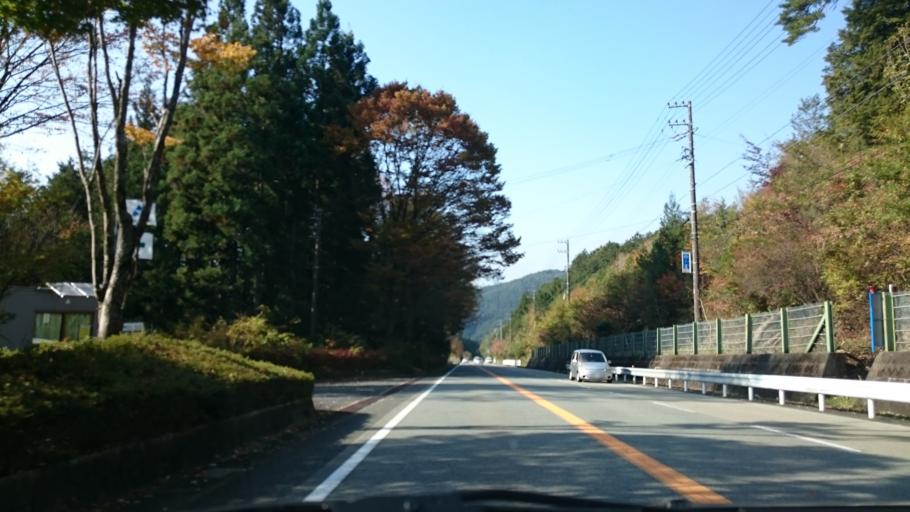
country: JP
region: Gifu
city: Nakatsugawa
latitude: 35.7575
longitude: 137.3264
